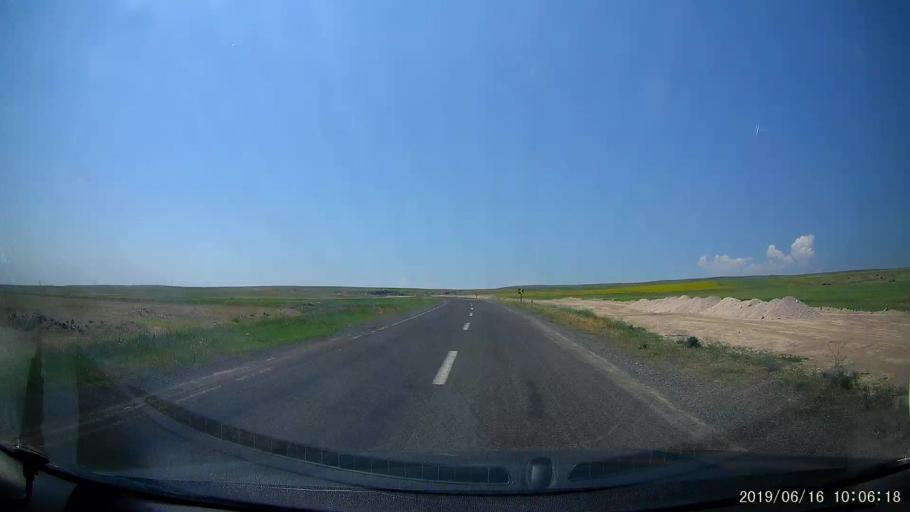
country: TR
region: Kars
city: Digor
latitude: 40.2574
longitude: 43.5416
